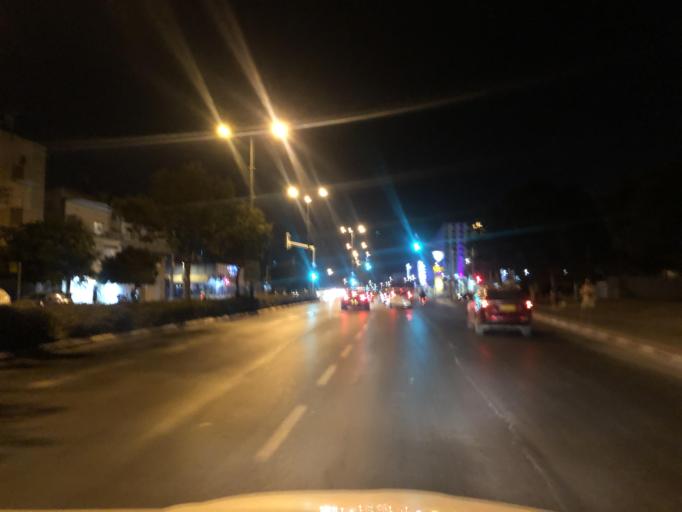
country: IL
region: Tel Aviv
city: Yafo
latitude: 32.0489
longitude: 34.7749
